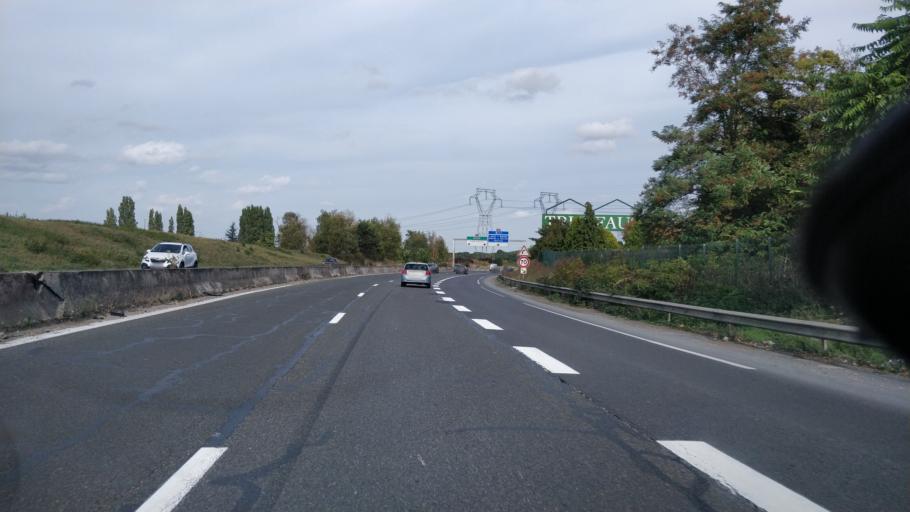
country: FR
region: Ile-de-France
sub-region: Departement de Seine-et-Marne
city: Villeparisis
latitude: 48.9386
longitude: 2.6226
